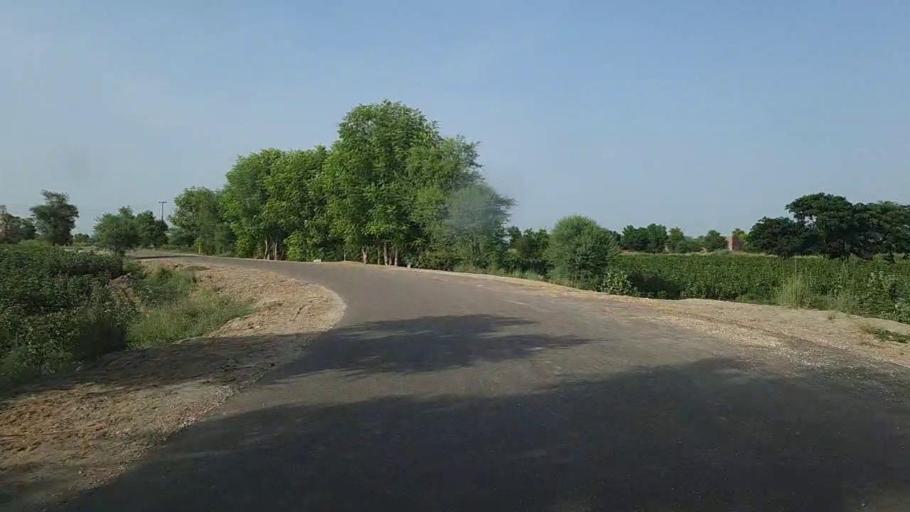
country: PK
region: Sindh
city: Ubauro
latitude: 28.1096
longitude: 69.8496
